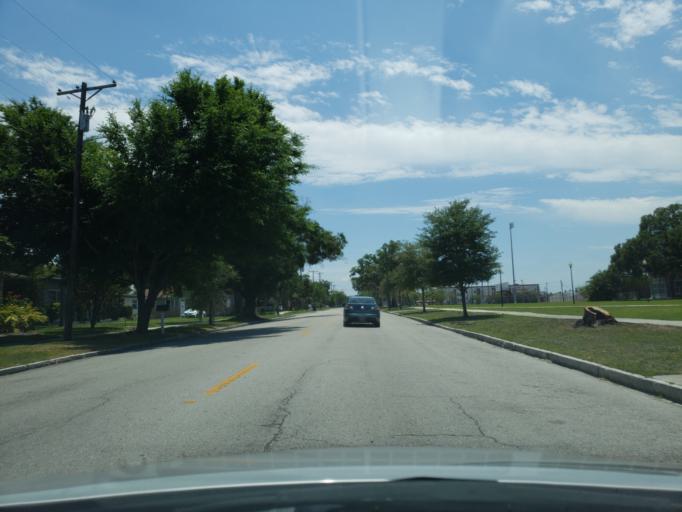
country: US
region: Florida
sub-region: Hillsborough County
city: Tampa
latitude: 27.9918
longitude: -82.4553
